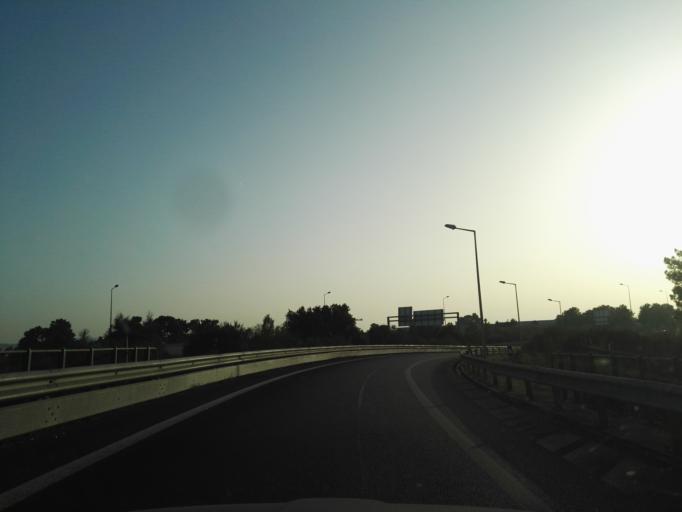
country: PT
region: Setubal
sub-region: Barreiro
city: Santo Antonio da Charneca
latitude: 38.5792
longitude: -9.0173
